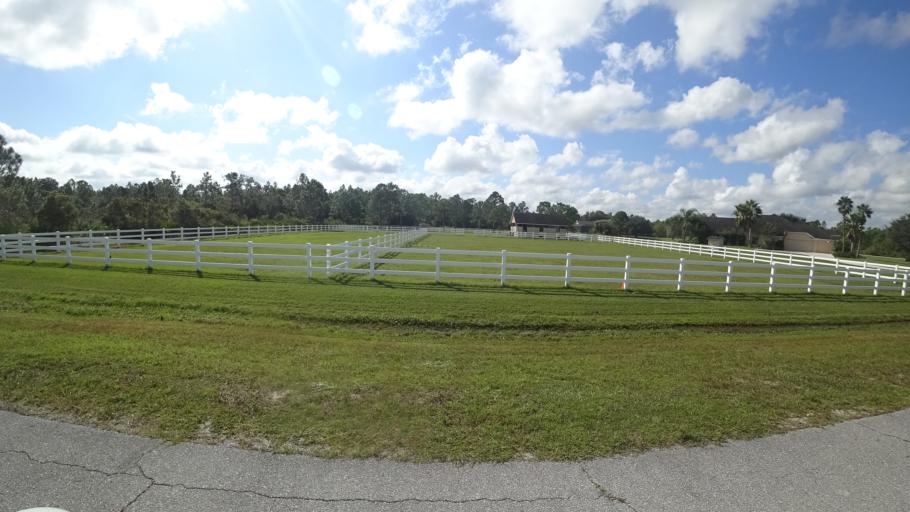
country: US
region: Florida
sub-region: Sarasota County
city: The Meadows
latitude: 27.4024
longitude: -82.3387
